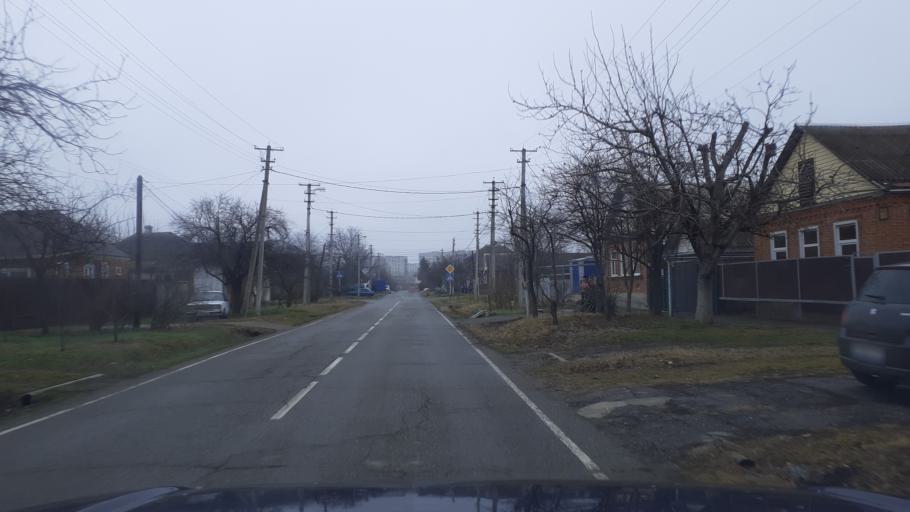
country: RU
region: Adygeya
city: Maykop
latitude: 44.6195
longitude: 40.0731
